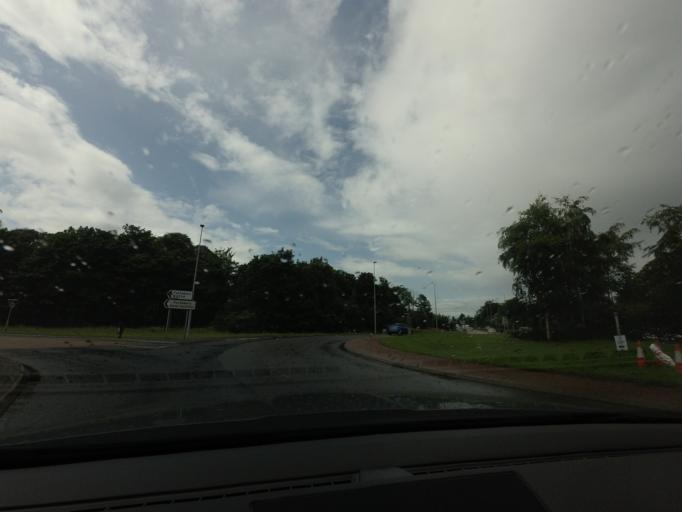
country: GB
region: Scotland
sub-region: Moray
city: Fochabers
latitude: 57.6188
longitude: -3.1037
